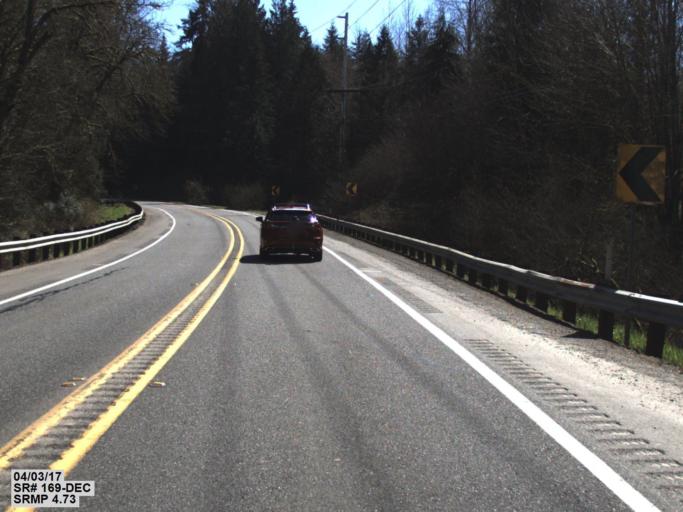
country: US
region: Washington
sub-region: King County
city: Black Diamond
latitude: 47.2698
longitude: -121.9933
